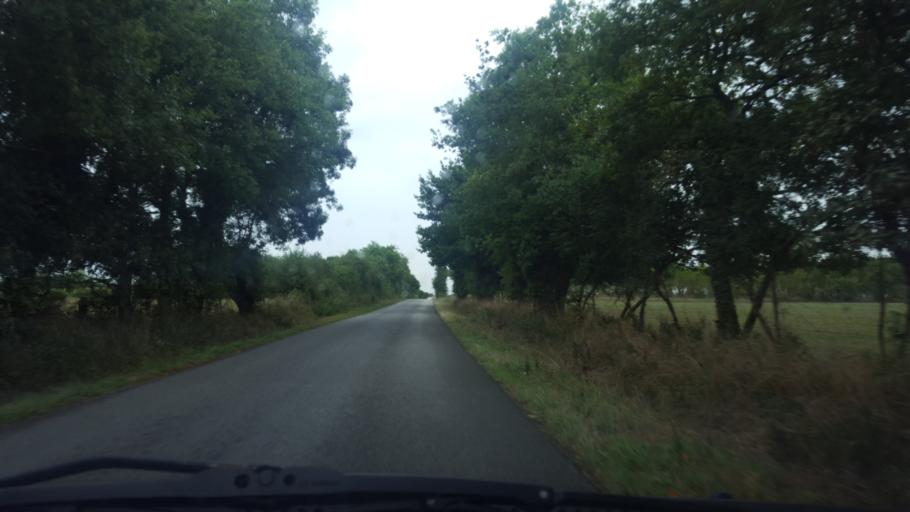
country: FR
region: Pays de la Loire
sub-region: Departement de la Loire-Atlantique
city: Saint-Lumine-de-Coutais
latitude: 47.0541
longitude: -1.7086
